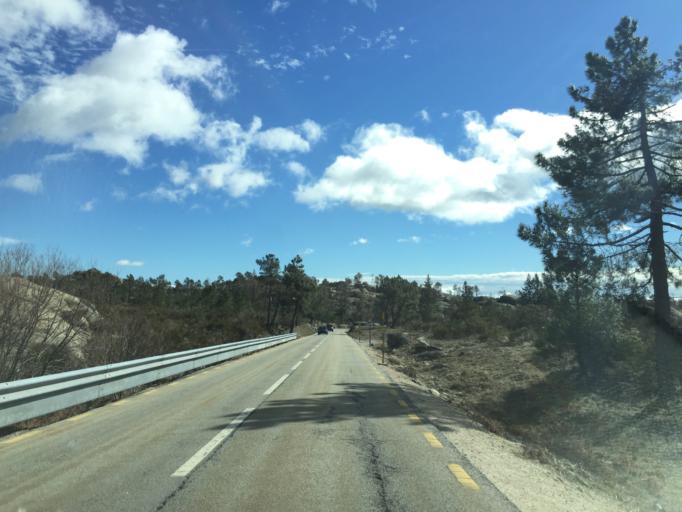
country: PT
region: Castelo Branco
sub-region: Covilha
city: Covilha
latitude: 40.3038
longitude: -7.5361
